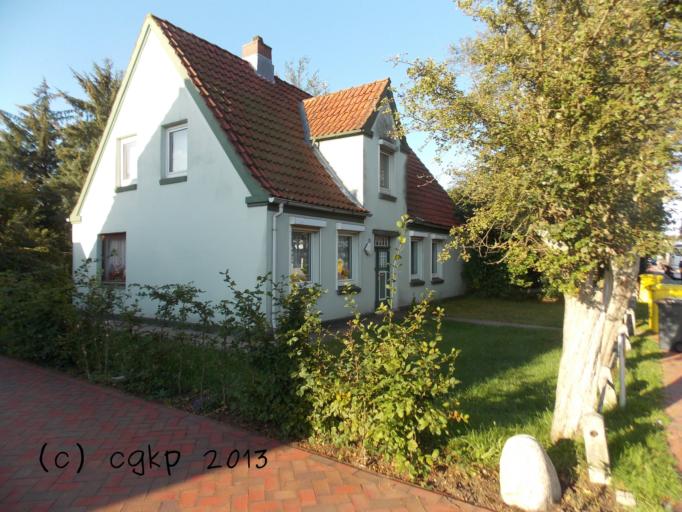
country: DE
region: Schleswig-Holstein
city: Sankt Peter-Ording
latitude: 54.3058
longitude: 8.6336
